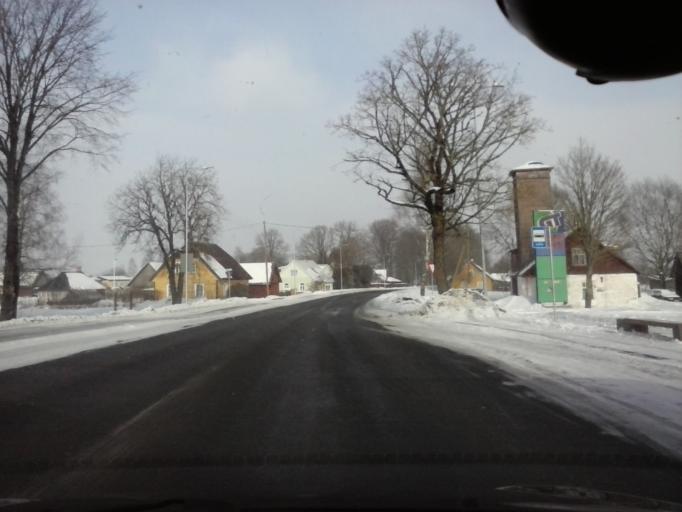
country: EE
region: Viljandimaa
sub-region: Abja vald
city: Abja-Paluoja
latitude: 58.3266
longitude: 25.3069
